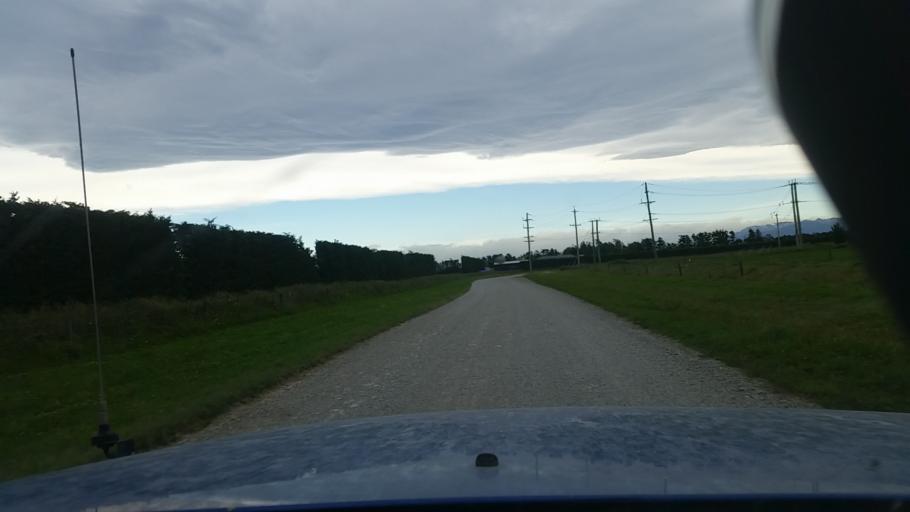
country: NZ
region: Canterbury
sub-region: Ashburton District
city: Tinwald
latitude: -44.0188
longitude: 171.5006
